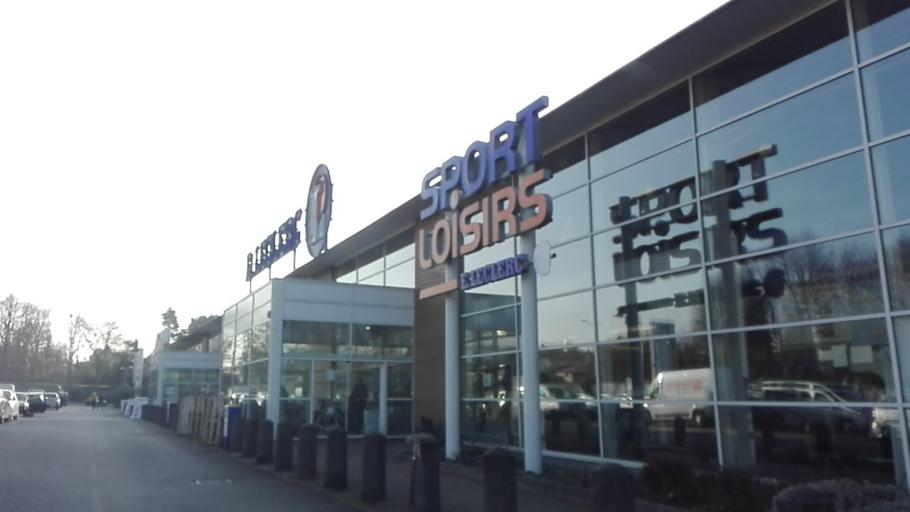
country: FR
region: Pays de la Loire
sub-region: Departement de la Vendee
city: Montaigu
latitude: 46.9754
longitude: -1.3042
